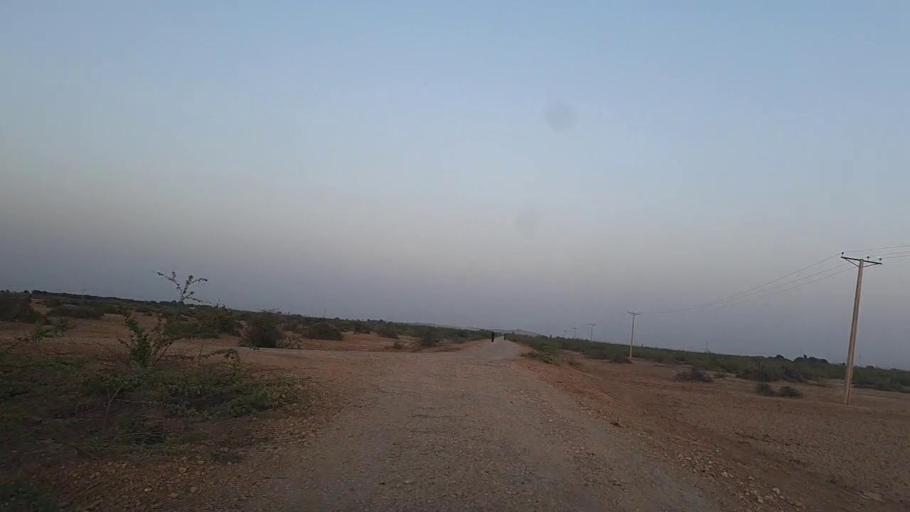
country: PK
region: Sindh
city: Naukot
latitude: 24.7200
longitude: 69.2911
